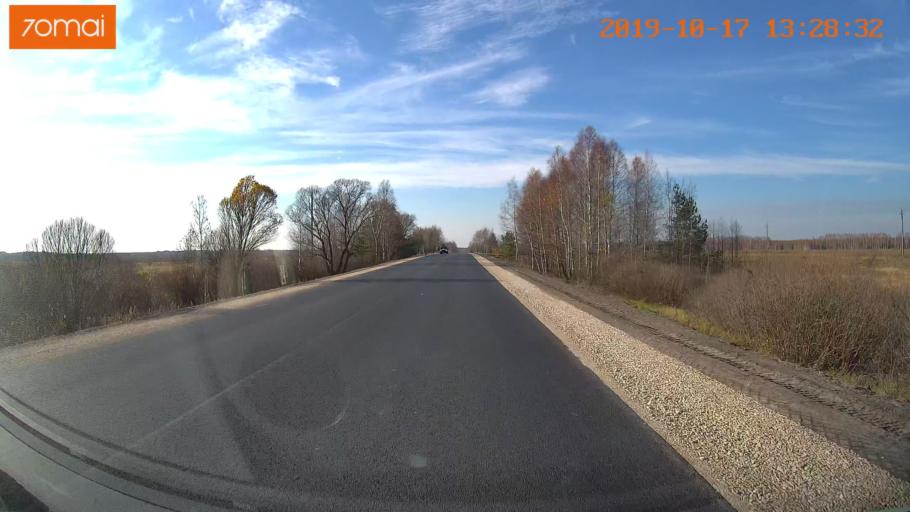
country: RU
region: Vladimir
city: Velikodvorskiy
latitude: 55.1165
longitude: 40.8660
